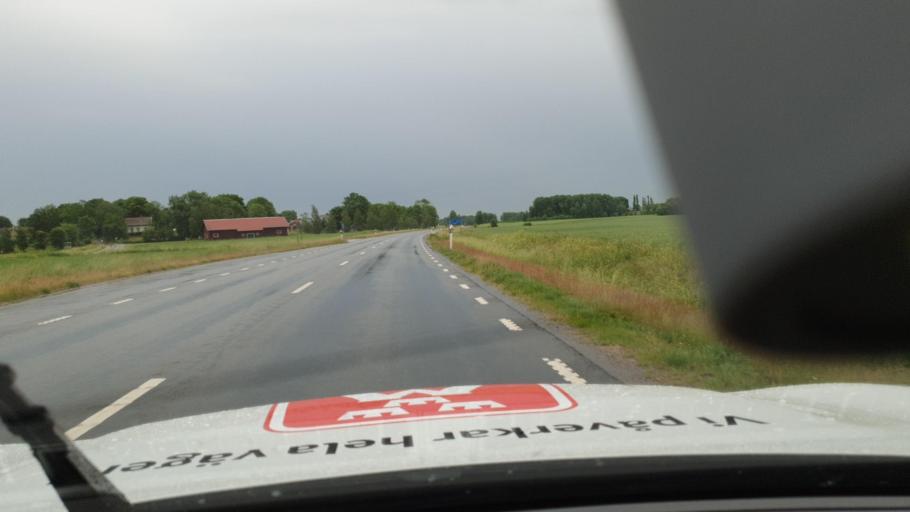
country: SE
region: Vaestra Goetaland
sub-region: Mariestads Kommun
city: Mariestad
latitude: 58.6629
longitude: 13.8772
